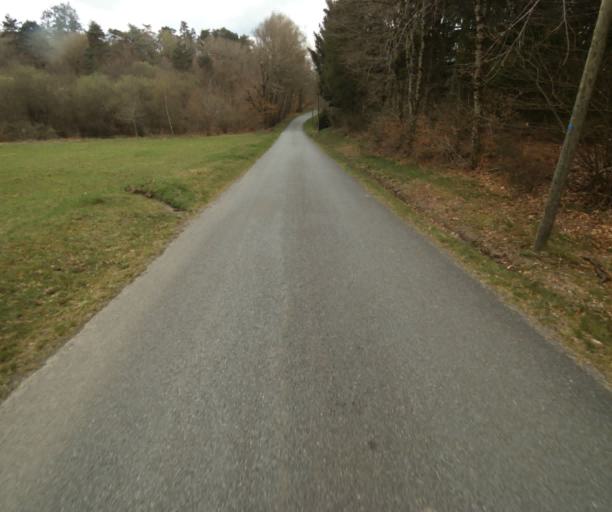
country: FR
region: Limousin
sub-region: Departement de la Correze
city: Correze
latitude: 45.3153
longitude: 1.9327
